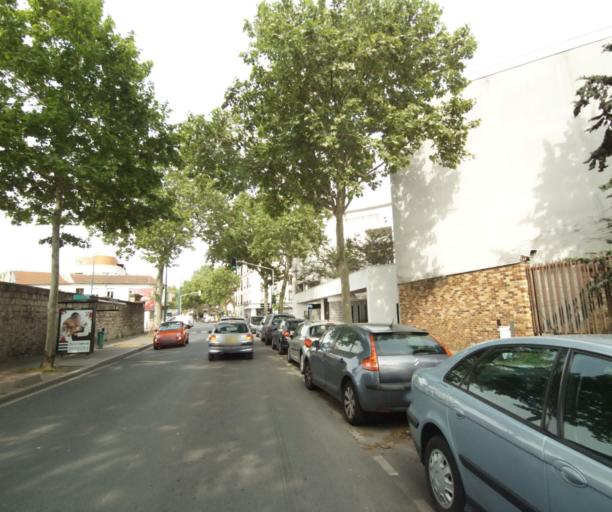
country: FR
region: Ile-de-France
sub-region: Departement des Hauts-de-Seine
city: Gennevilliers
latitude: 48.9283
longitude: 2.2990
